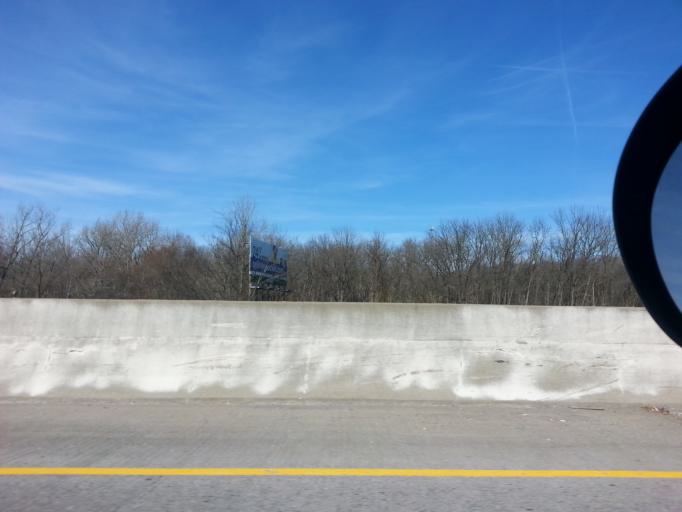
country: US
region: Tennessee
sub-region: Rutherford County
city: La Vergne
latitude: 36.0516
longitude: -86.6700
